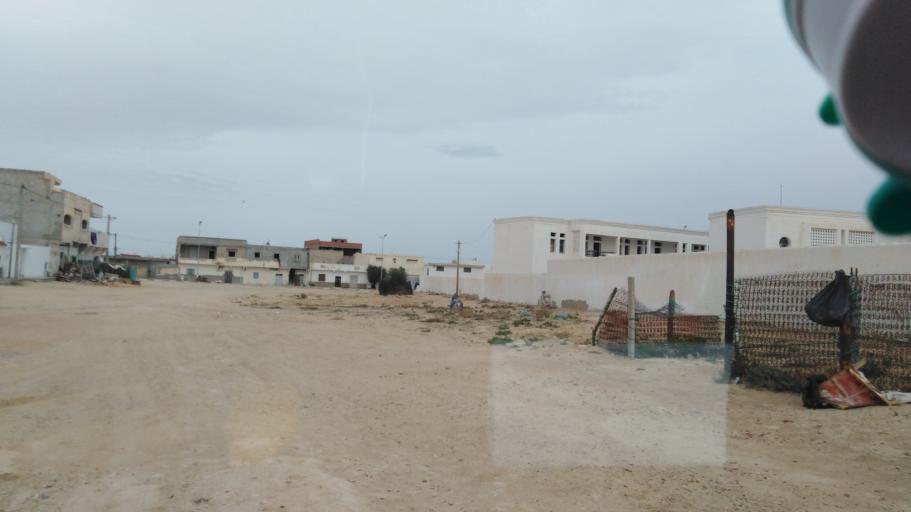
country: TN
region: Qabis
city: Gabes
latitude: 33.9487
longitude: 10.0037
